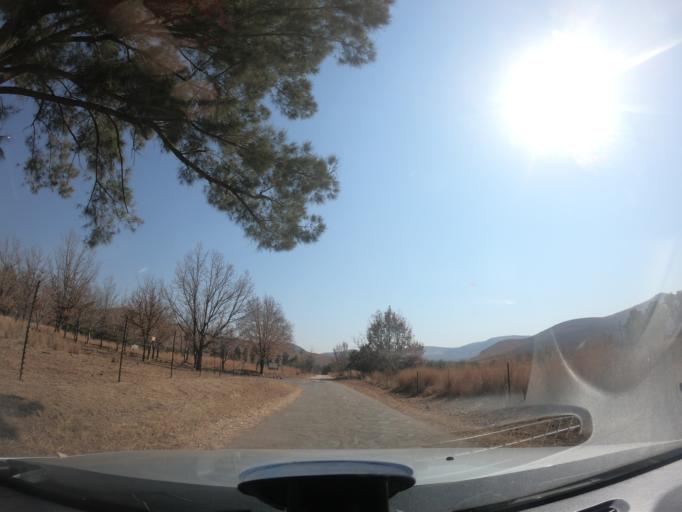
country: ZA
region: Gauteng
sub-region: City of Johannesburg Metropolitan Municipality
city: Diepsloot
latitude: -25.8325
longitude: 28.0288
